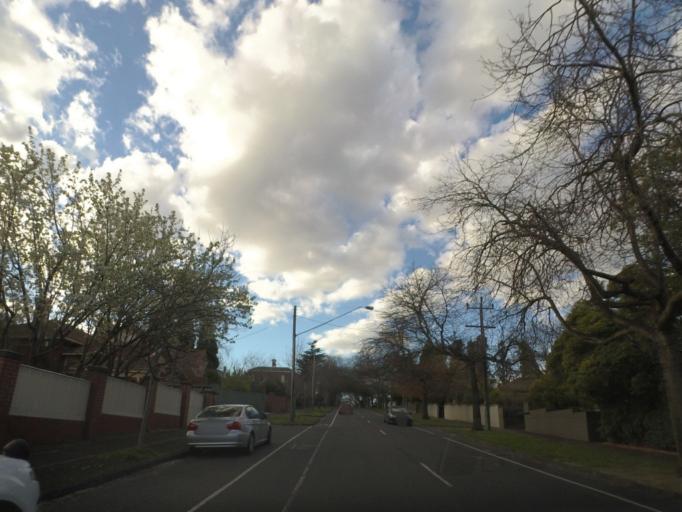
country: AU
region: Victoria
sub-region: Boroondara
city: Canterbury
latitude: -37.8232
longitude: 145.0793
